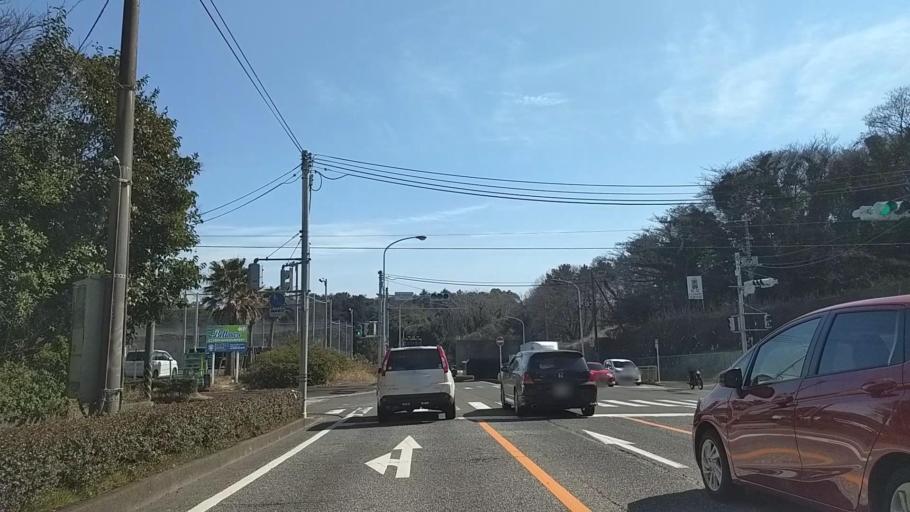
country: JP
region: Kanagawa
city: Fujisawa
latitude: 35.3534
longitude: 139.4438
